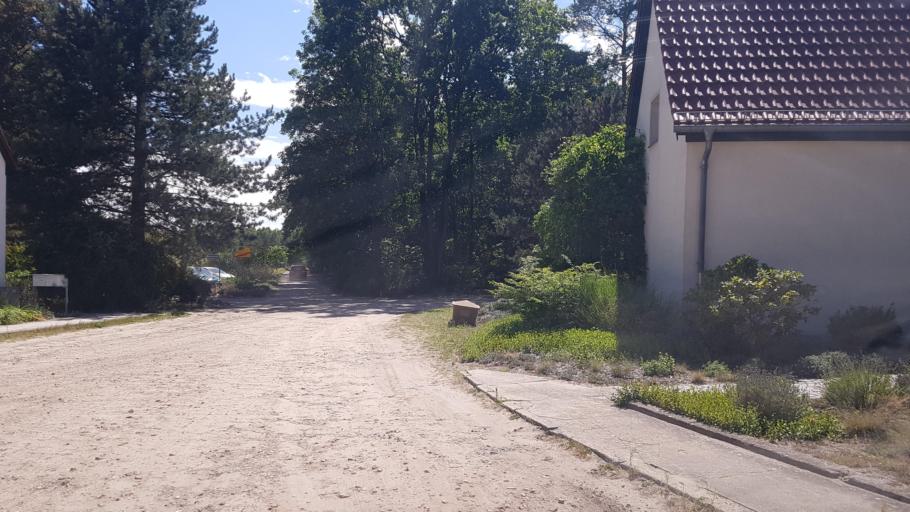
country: DE
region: Brandenburg
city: Trebbin
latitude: 52.2424
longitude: 13.1466
